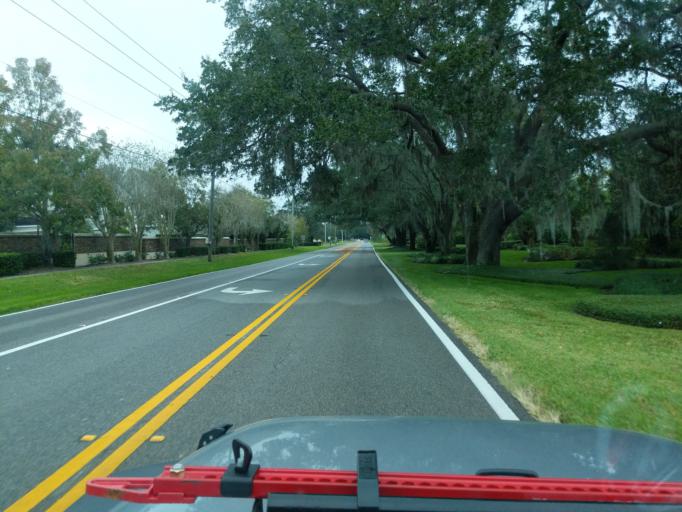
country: US
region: Florida
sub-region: Orange County
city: Winter Garden
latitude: 28.5284
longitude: -81.5909
